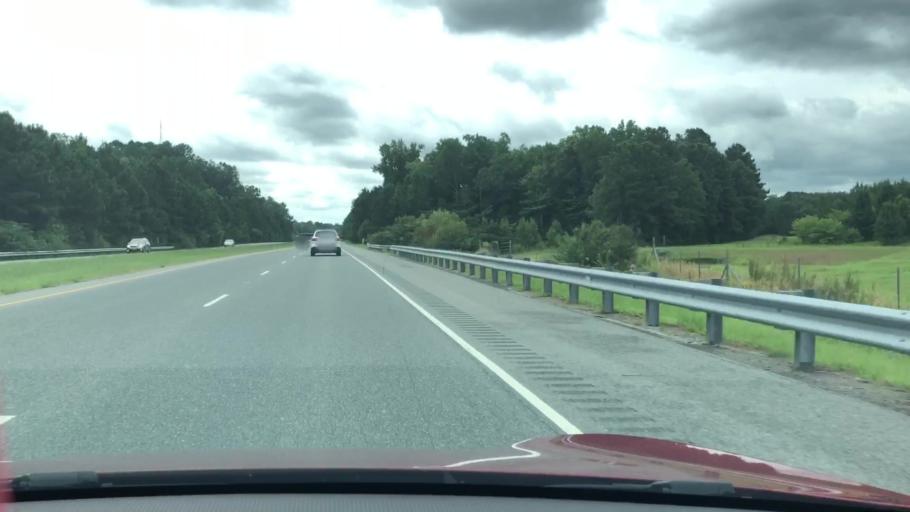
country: US
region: North Carolina
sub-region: Currituck County
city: Moyock
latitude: 36.6399
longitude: -76.2188
